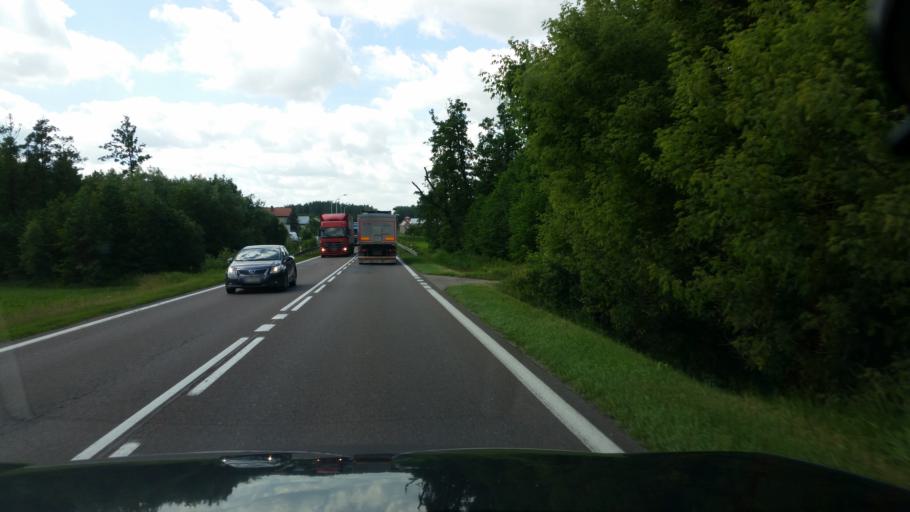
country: PL
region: Podlasie
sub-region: Powiat grajewski
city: Szczuczyn
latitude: 53.5285
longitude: 22.2568
